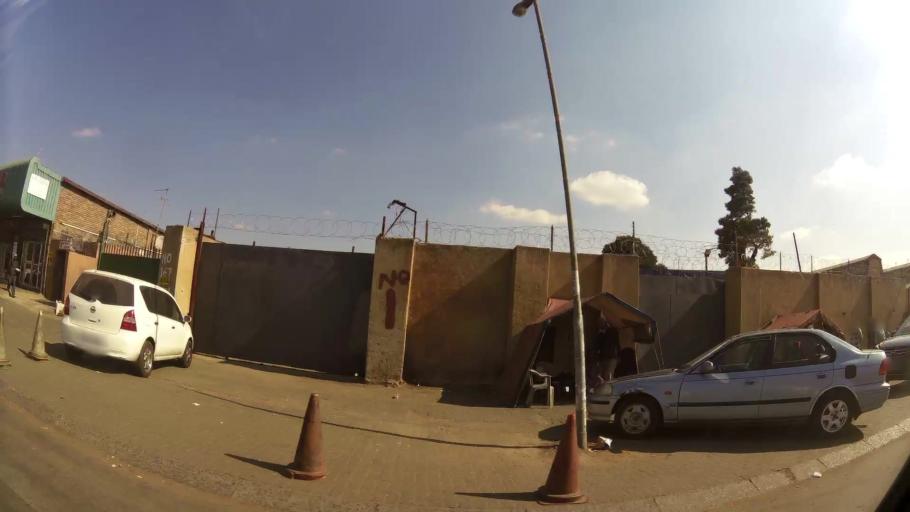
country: ZA
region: Gauteng
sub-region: Ekurhuleni Metropolitan Municipality
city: Boksburg
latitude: -26.2077
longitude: 28.2846
